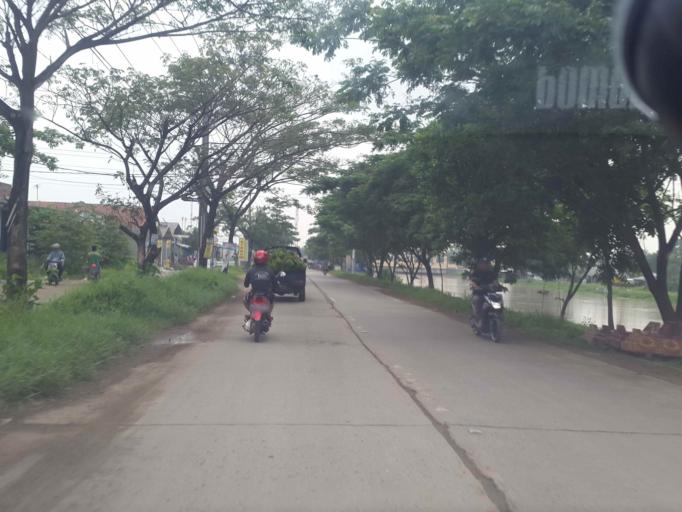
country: ID
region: West Java
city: Cikarang
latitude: -6.3313
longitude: 107.1782
